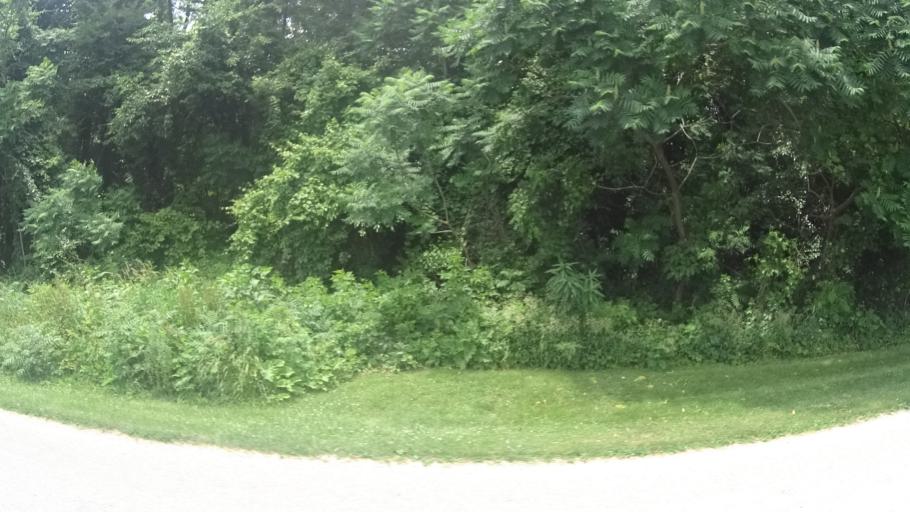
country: US
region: Ohio
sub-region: Erie County
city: Milan
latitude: 41.3034
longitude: -82.6319
